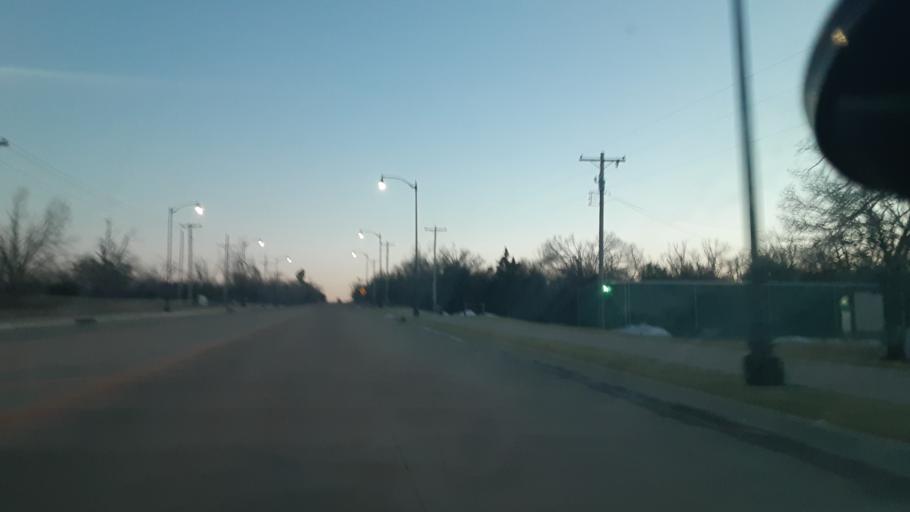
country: US
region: Oklahoma
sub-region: Oklahoma County
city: Edmond
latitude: 35.6797
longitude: -97.4251
